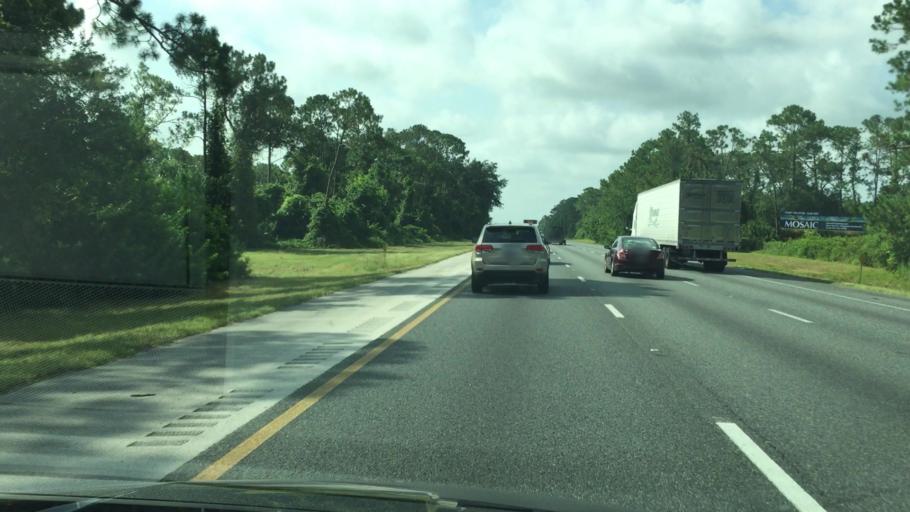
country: US
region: Florida
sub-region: Volusia County
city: Ormond Beach
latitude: 29.2815
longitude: -81.1249
